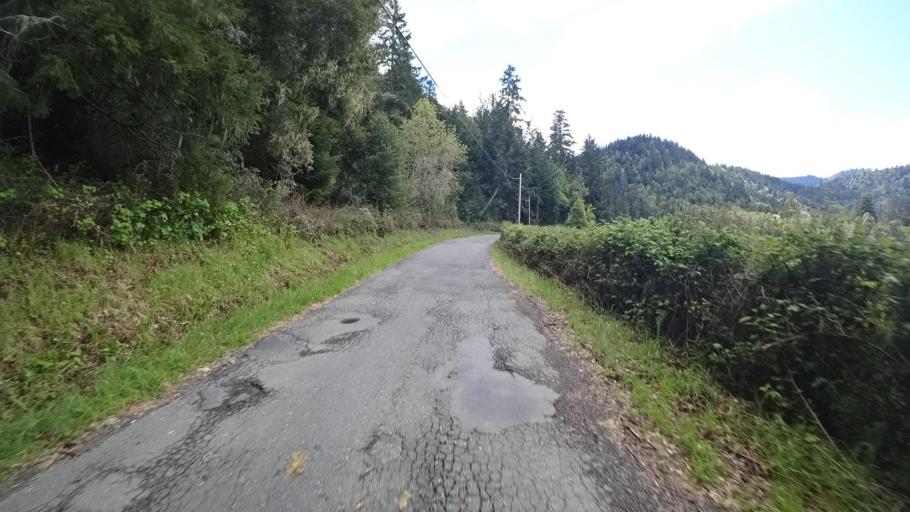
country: US
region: California
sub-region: Humboldt County
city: Blue Lake
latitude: 40.7665
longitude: -123.8949
